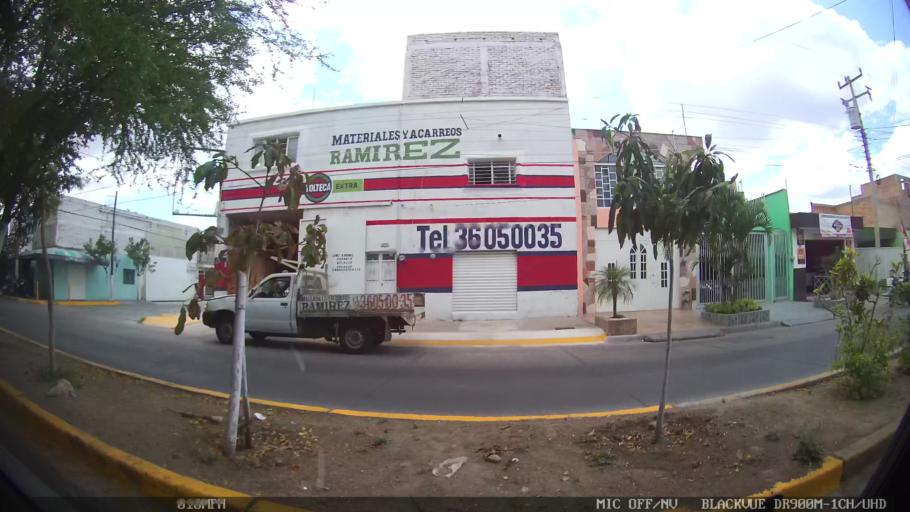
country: MX
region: Jalisco
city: Tlaquepaque
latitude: 20.6539
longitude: -103.2825
